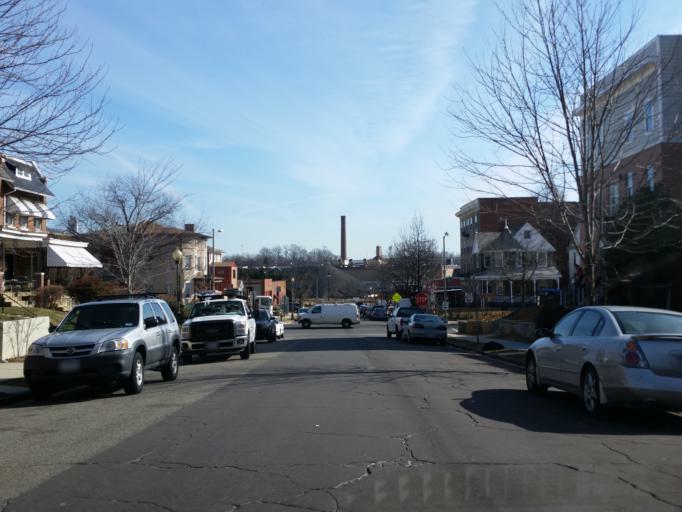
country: US
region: Washington, D.C.
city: Washington, D.C.
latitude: 38.9140
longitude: -77.0029
